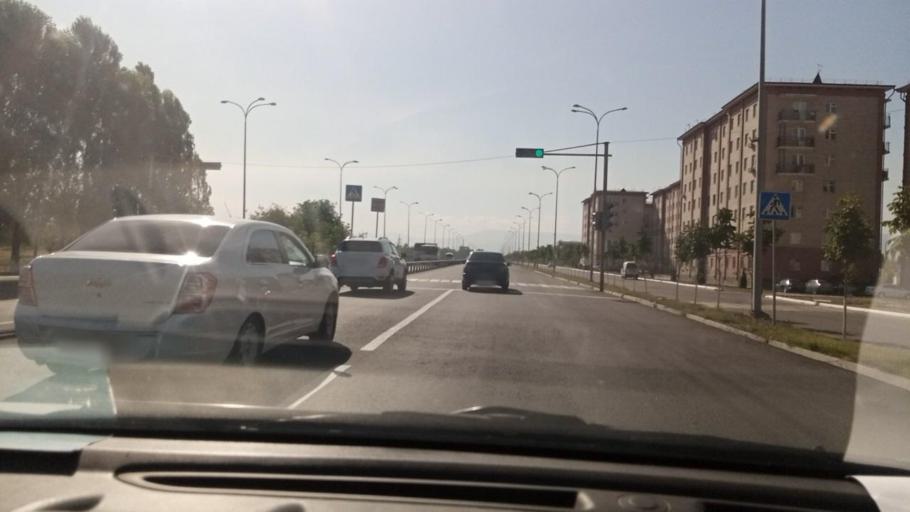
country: UZ
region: Toshkent
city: Ohangaron
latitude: 40.9144
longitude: 69.6093
